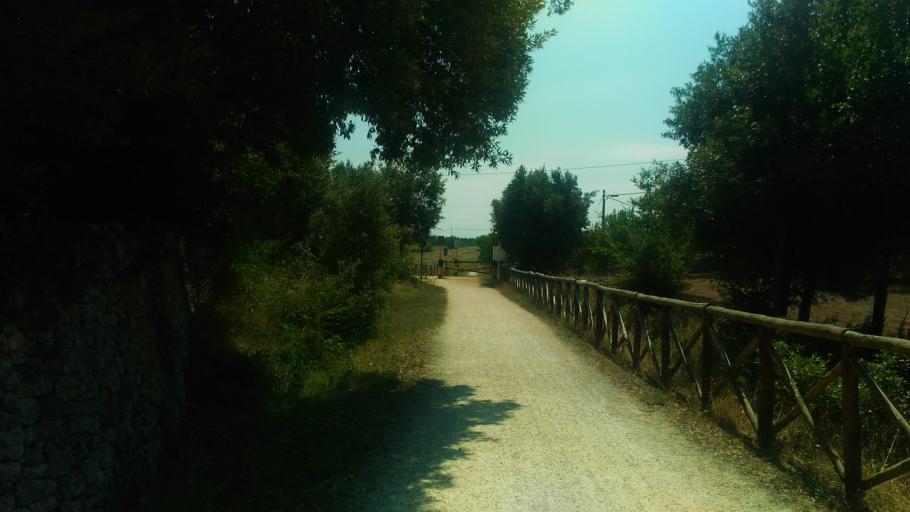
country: IT
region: Apulia
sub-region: Provincia di Brindisi
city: Cisternino
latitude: 40.7245
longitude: 17.3961
